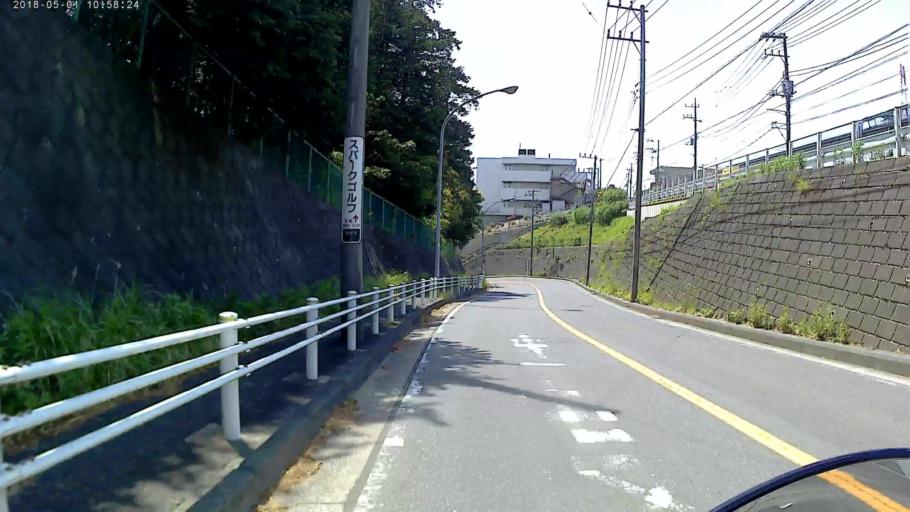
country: JP
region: Kanagawa
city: Minami-rinkan
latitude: 35.4797
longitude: 139.5110
